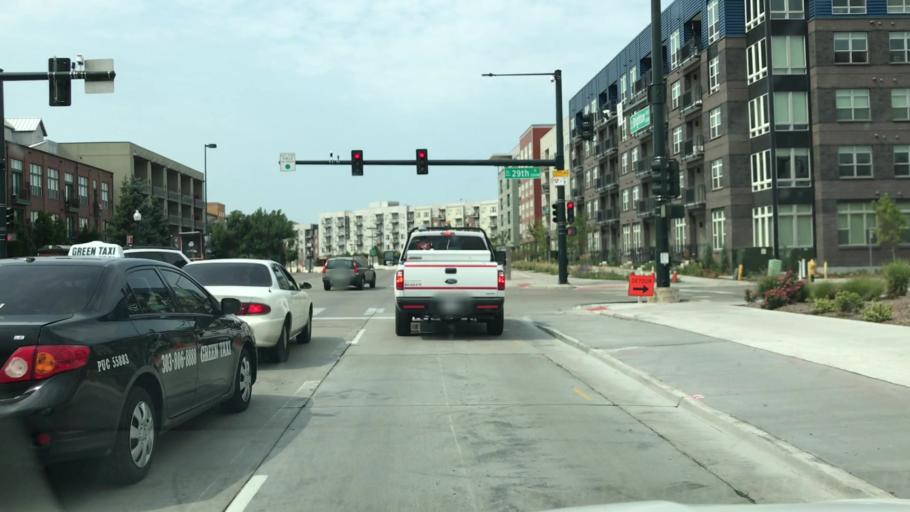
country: US
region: Colorado
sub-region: Denver County
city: Denver
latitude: 39.7646
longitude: -104.9863
